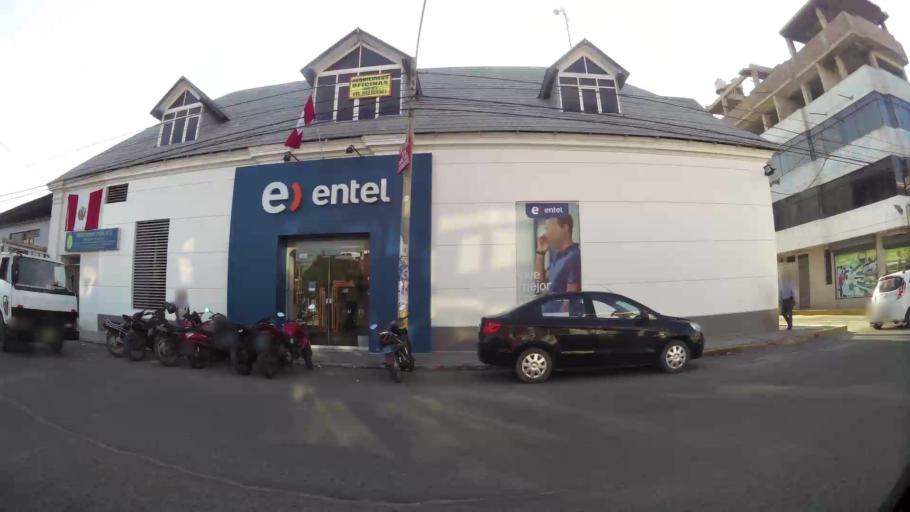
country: PE
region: Lambayeque
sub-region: Provincia de Chiclayo
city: Chiclayo
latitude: -6.7757
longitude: -79.8427
